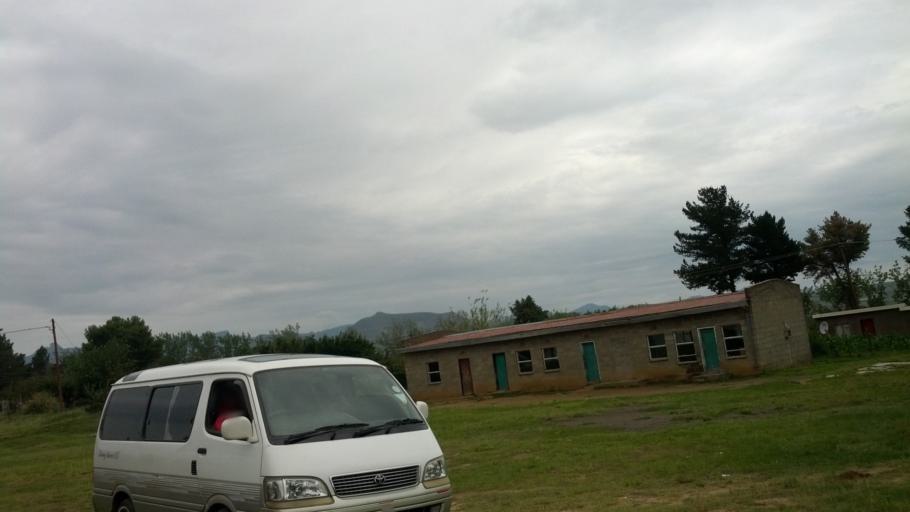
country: LS
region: Berea
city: Teyateyaneng
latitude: -29.1050
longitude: 27.9606
